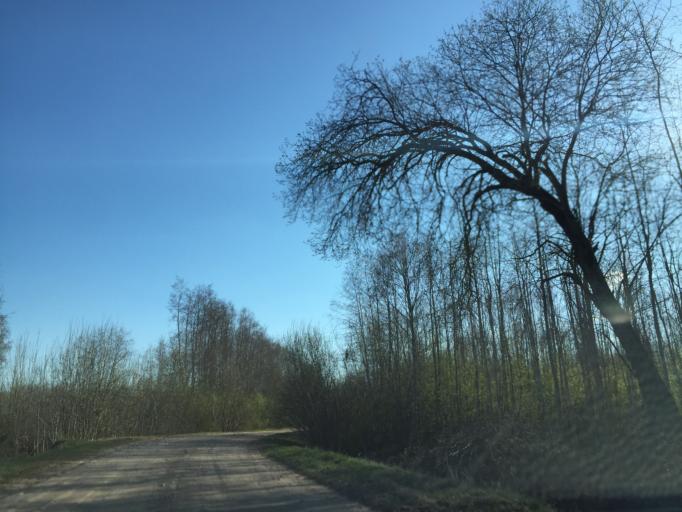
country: EE
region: Valgamaa
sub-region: Torva linn
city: Torva
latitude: 58.2328
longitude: 25.9285
